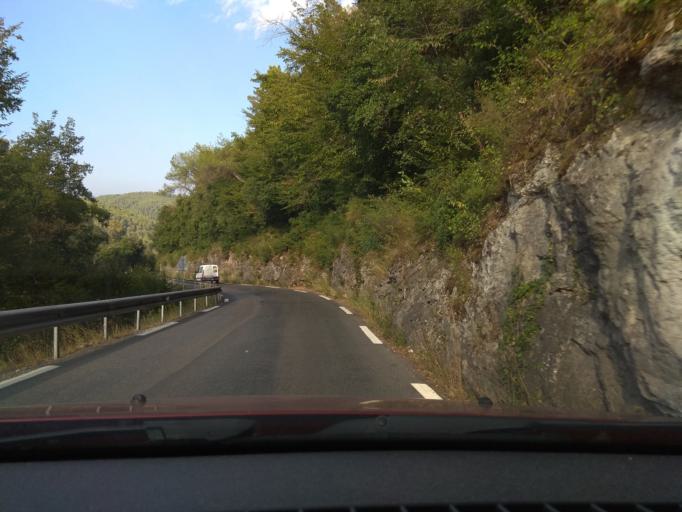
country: FR
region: Provence-Alpes-Cote d'Azur
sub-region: Departement des Alpes-Maritimes
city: Tourrettes-sur-Loup
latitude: 43.6837
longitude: 7.0593
